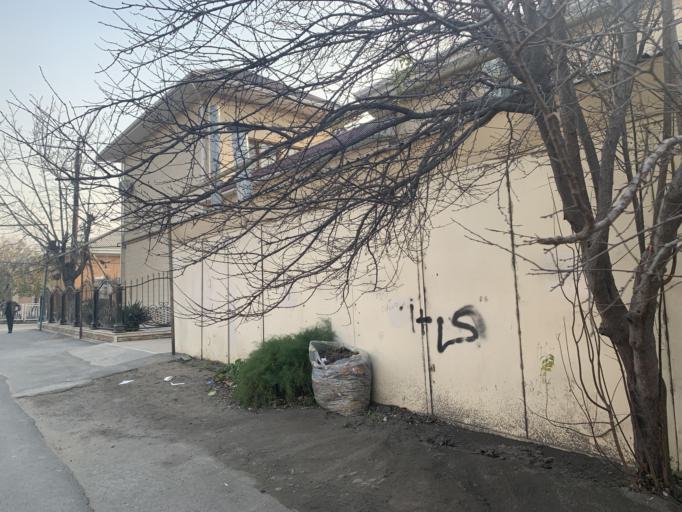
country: UZ
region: Fergana
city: Qo`qon
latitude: 40.5448
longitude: 70.9268
